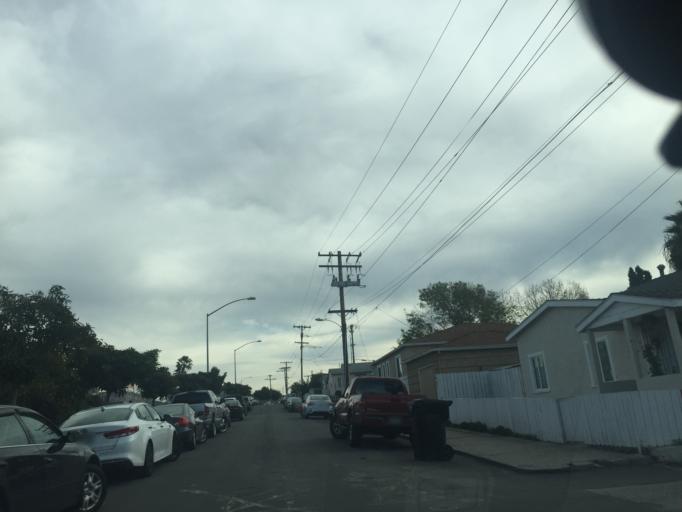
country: US
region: California
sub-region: San Diego County
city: Lemon Grove
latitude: 32.7514
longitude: -117.0897
